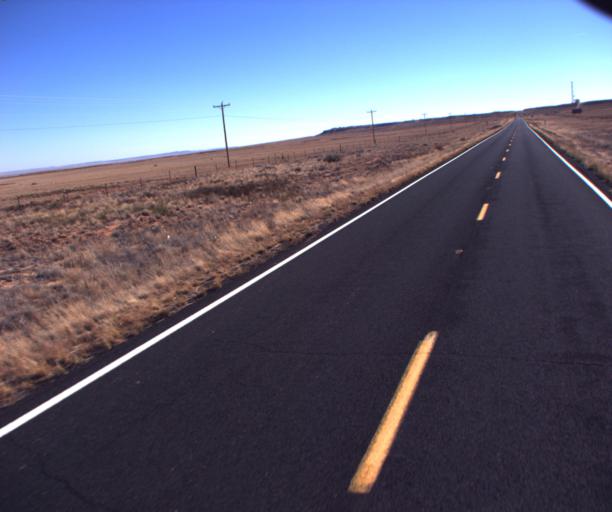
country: US
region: Arizona
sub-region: Coconino County
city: Tuba City
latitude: 36.0015
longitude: -111.0393
